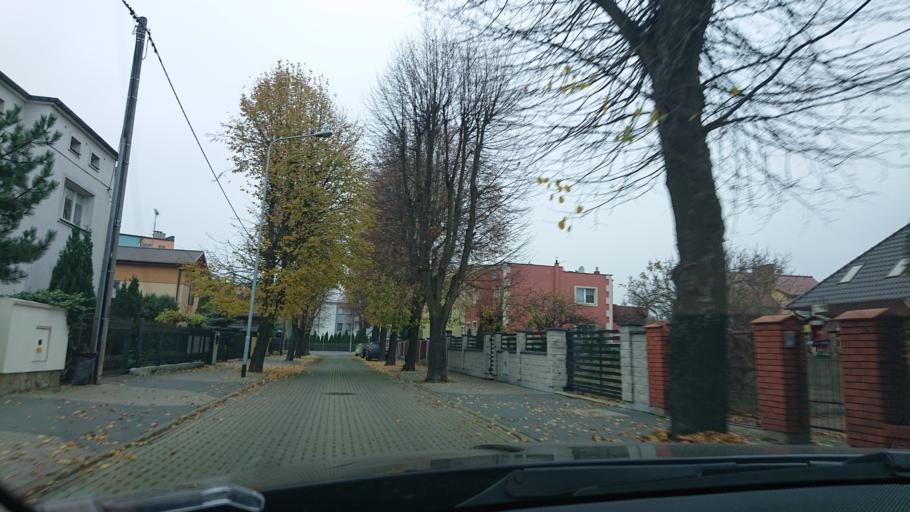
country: PL
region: Greater Poland Voivodeship
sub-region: Powiat gnieznienski
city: Gniezno
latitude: 52.5338
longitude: 17.6205
